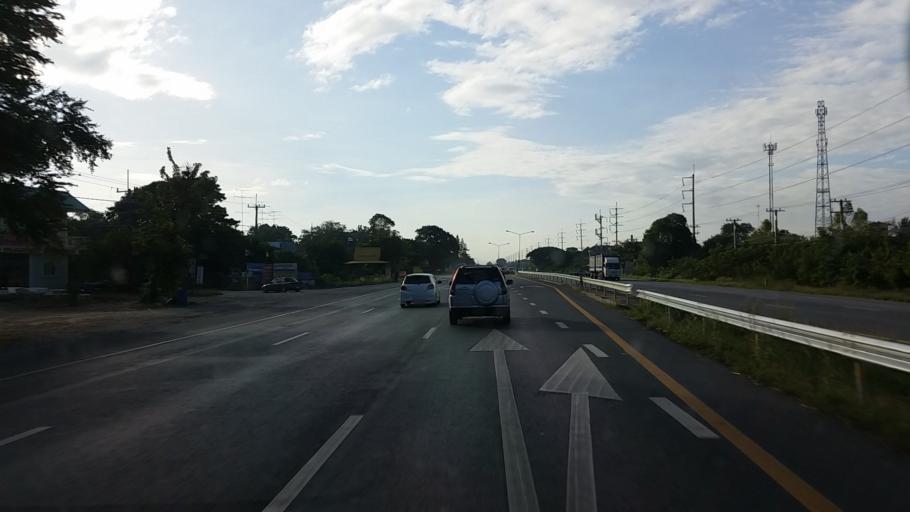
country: TH
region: Sara Buri
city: Chaloem Phra Kiat
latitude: 14.6242
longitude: 100.8906
